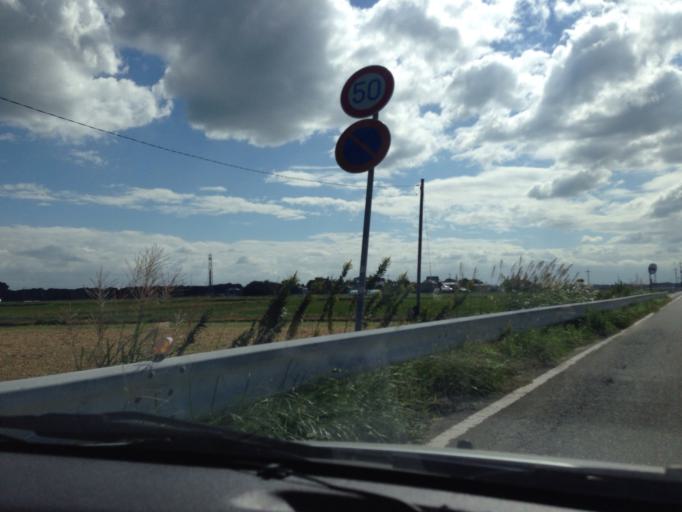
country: JP
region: Ibaraki
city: Inashiki
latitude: 36.0086
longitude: 140.3651
